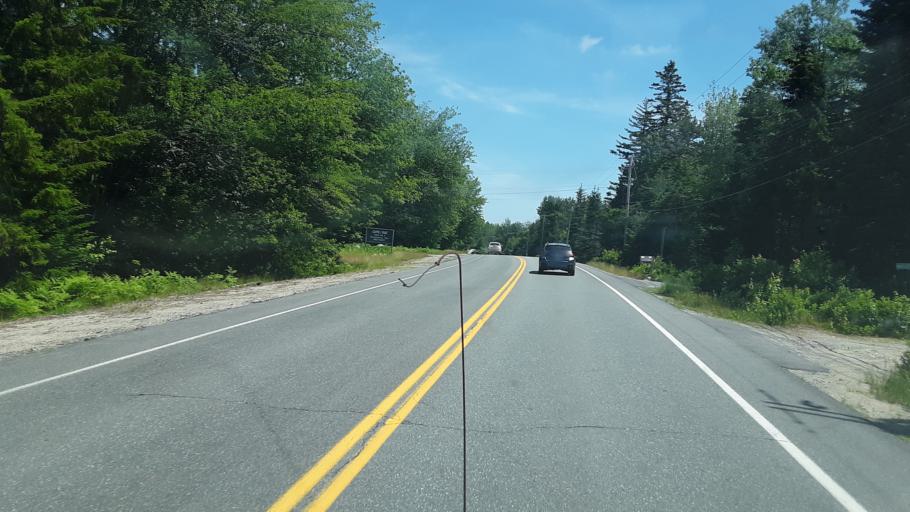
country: US
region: Maine
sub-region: Hancock County
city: Gouldsboro
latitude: 44.4715
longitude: -68.0942
